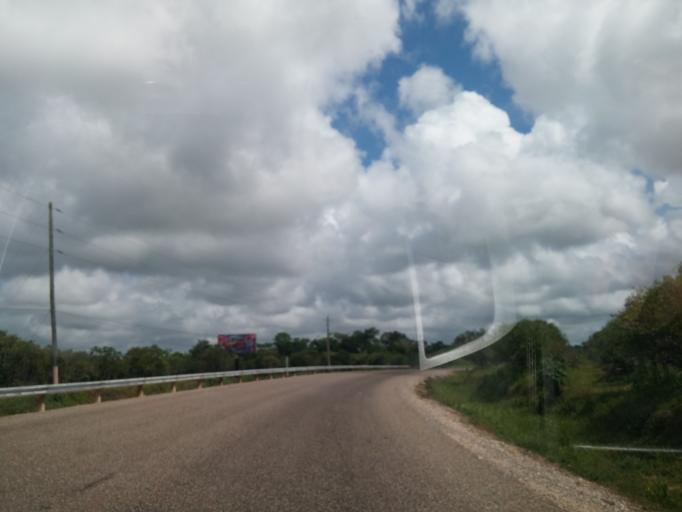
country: BZ
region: Stann Creek
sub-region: Dangriga
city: Dangriga
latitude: 16.9810
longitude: -88.2951
